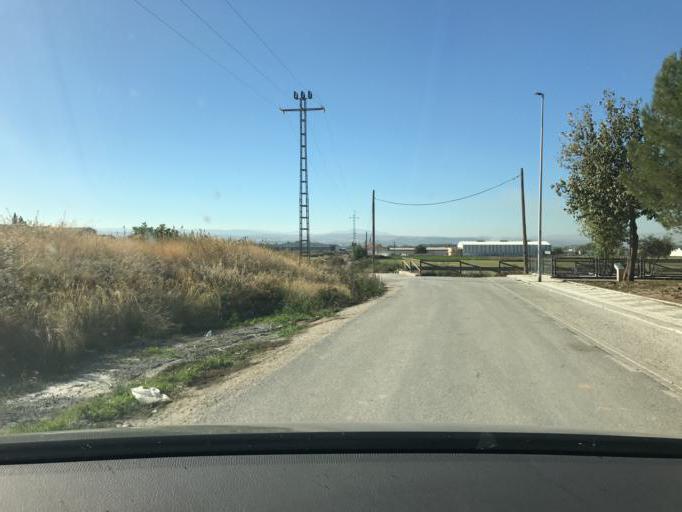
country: ES
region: Andalusia
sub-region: Provincia de Granada
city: Maracena
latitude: 37.2054
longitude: -3.6428
